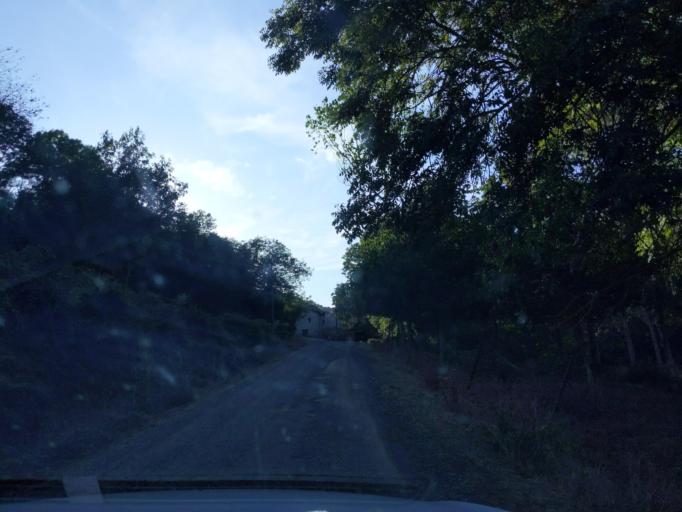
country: ES
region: La Rioja
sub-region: Provincia de La Rioja
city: Ojacastro
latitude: 42.3751
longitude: -3.0008
